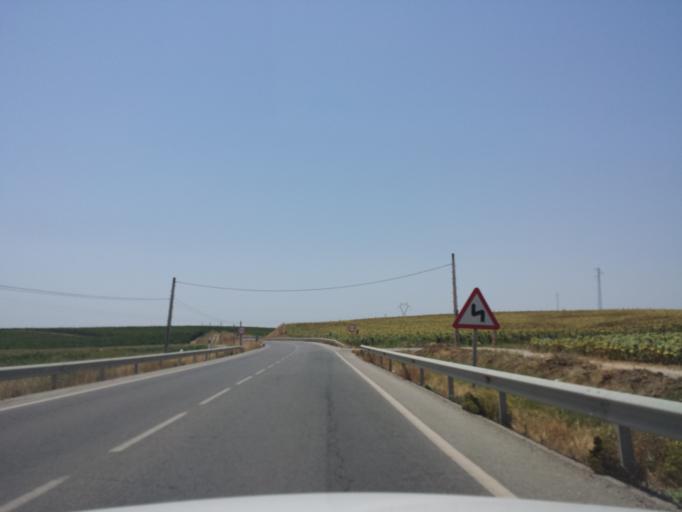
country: ES
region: Andalusia
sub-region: Provincia de Sevilla
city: Acala del Rio
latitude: 37.5340
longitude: -5.9589
